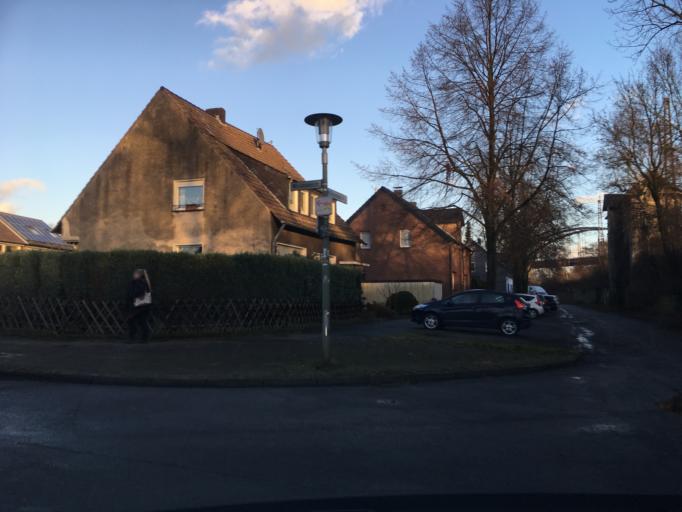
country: DE
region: North Rhine-Westphalia
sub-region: Regierungsbezirk Munster
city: Bottrop
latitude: 51.5037
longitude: 6.9247
